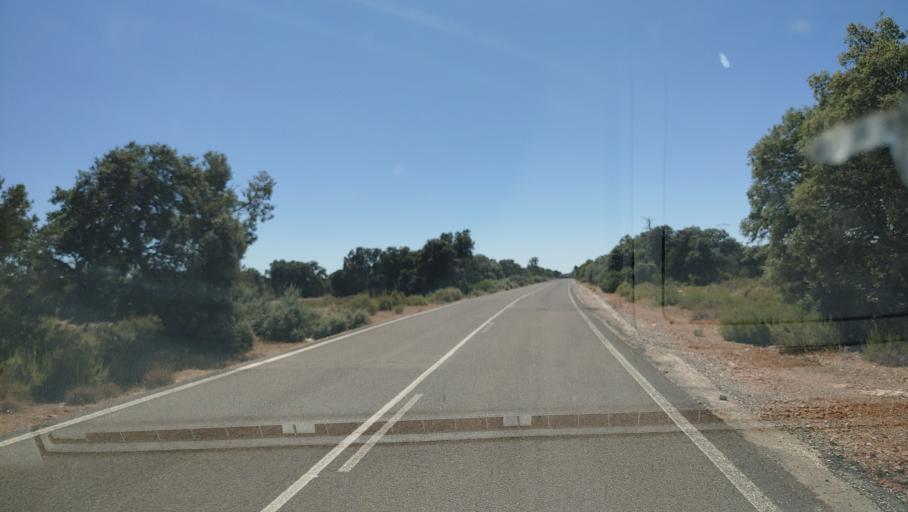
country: ES
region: Castille-La Mancha
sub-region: Provincia de Ciudad Real
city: Villahermosa
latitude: 38.8442
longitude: -2.8098
